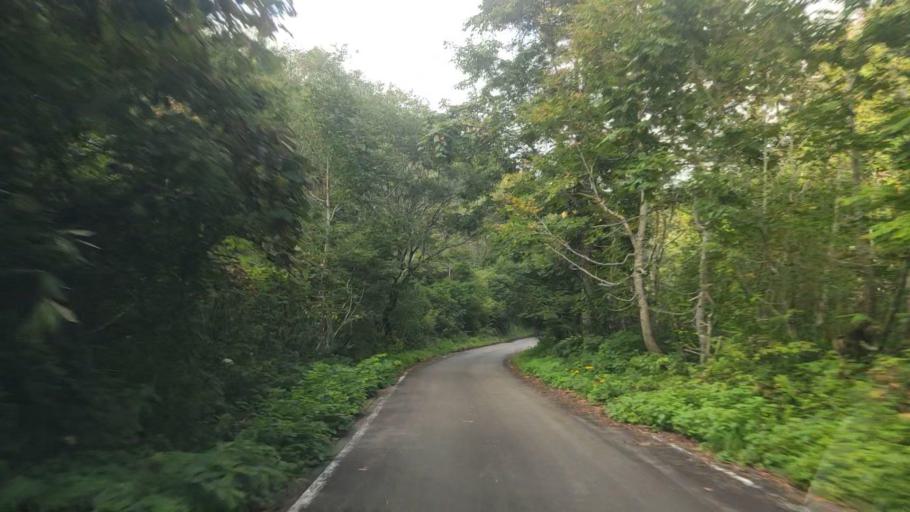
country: JP
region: Toyama
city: Yatsuomachi-higashikumisaka
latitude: 36.3772
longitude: 137.0812
